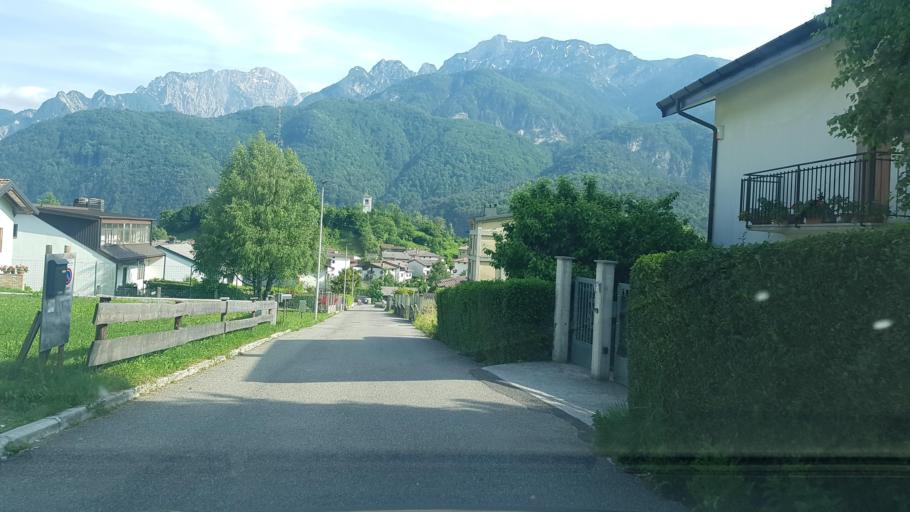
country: IT
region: Friuli Venezia Giulia
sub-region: Provincia di Udine
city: Moggio di Sotto
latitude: 46.4084
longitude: 13.1880
